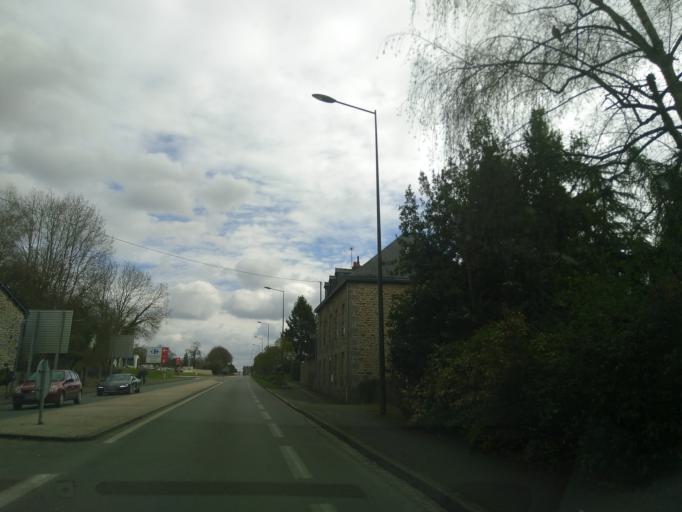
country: FR
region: Pays de la Loire
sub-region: Departement de la Mayenne
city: Mayenne
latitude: 48.3082
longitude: -0.6320
